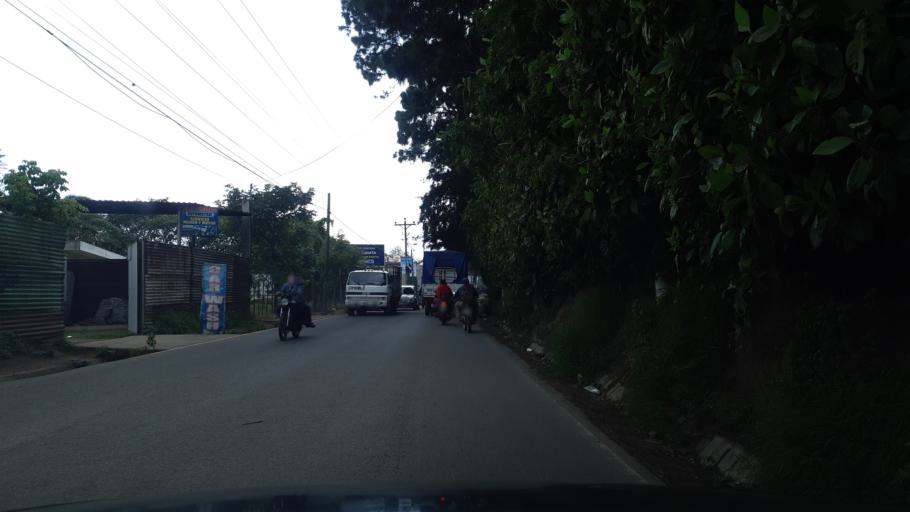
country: GT
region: Chimaltenango
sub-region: Municipio de Chimaltenango
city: Chimaltenango
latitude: 14.6668
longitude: -90.8081
